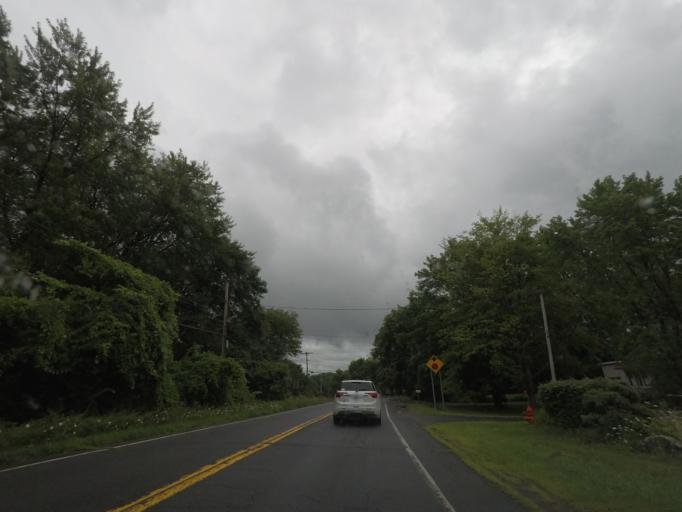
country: US
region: New York
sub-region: Rensselaer County
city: Hampton Manor
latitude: 42.6300
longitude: -73.7301
